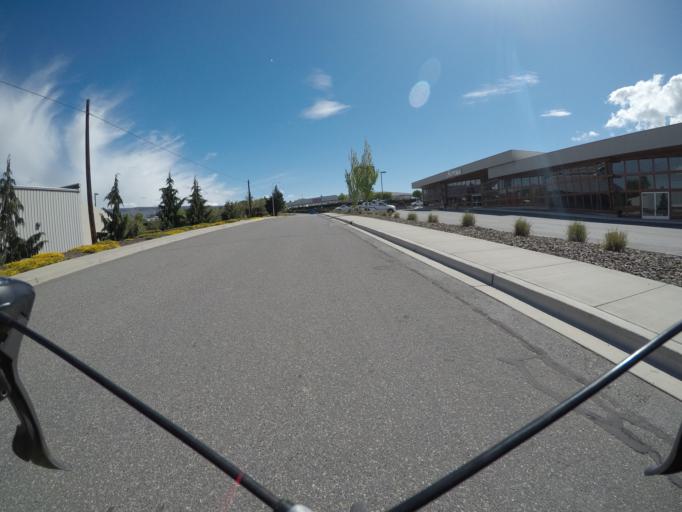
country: US
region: Washington
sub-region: Chelan County
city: South Wenatchee
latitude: 47.4019
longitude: -120.2838
